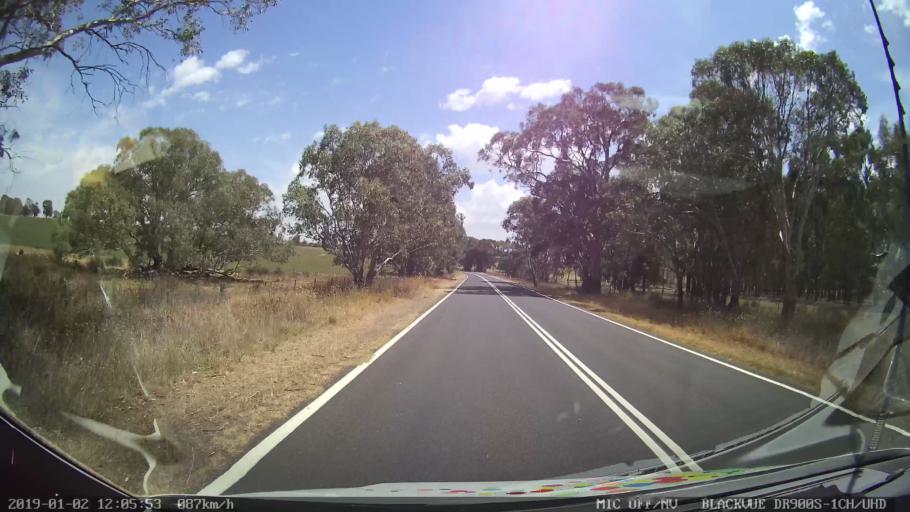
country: AU
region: New South Wales
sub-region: Young
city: Young
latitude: -34.5092
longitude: 148.2989
